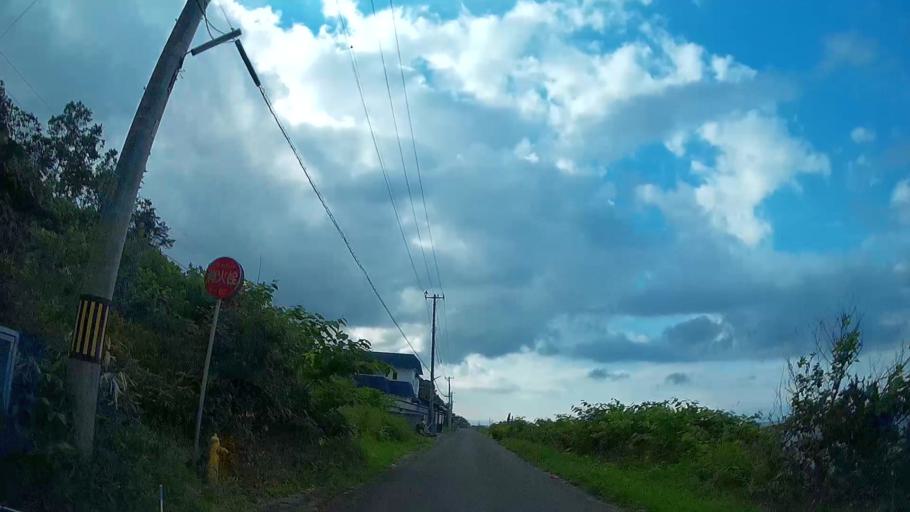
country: JP
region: Hokkaido
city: Nanae
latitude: 42.1168
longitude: 140.5415
